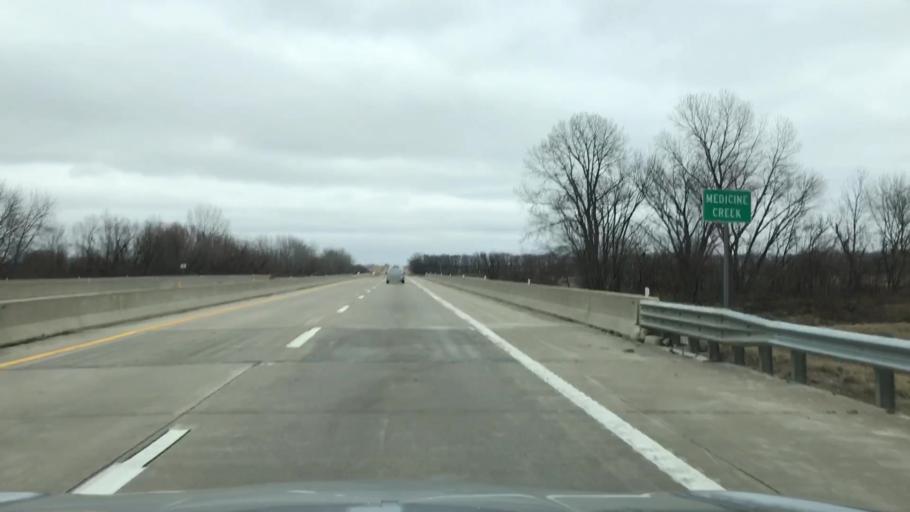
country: US
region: Missouri
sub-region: Livingston County
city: Chillicothe
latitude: 39.7767
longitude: -93.4259
